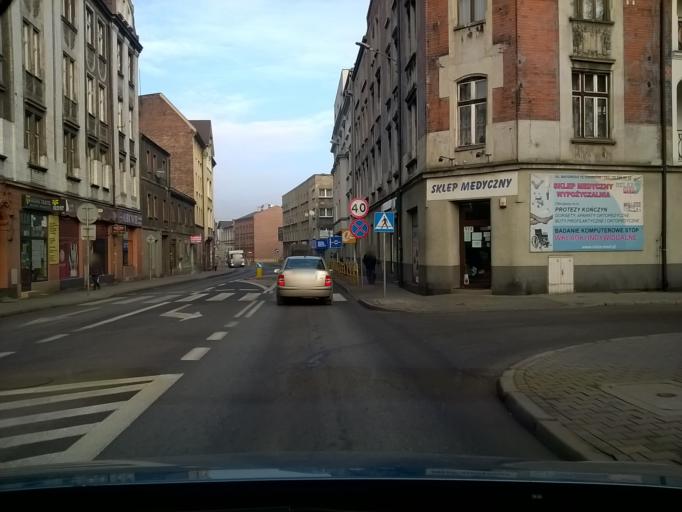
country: PL
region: Silesian Voivodeship
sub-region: Swietochlowice
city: Swietochlowice
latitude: 50.2746
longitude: 18.9396
